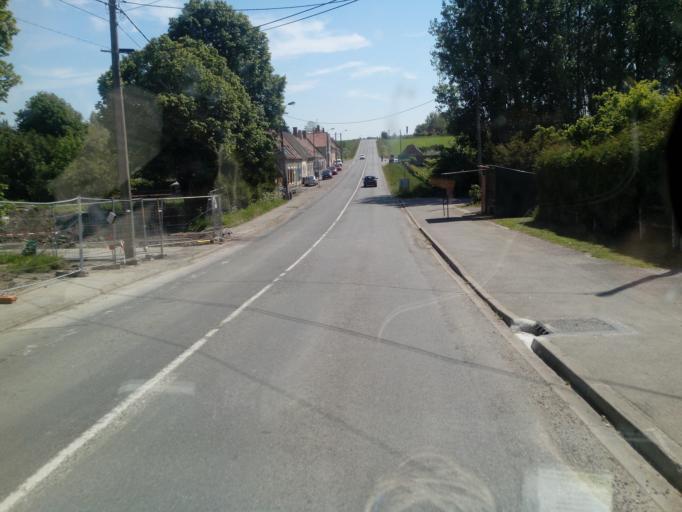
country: FR
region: Nord-Pas-de-Calais
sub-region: Departement du Pas-de-Calais
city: Samer
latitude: 50.6350
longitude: 1.7427
